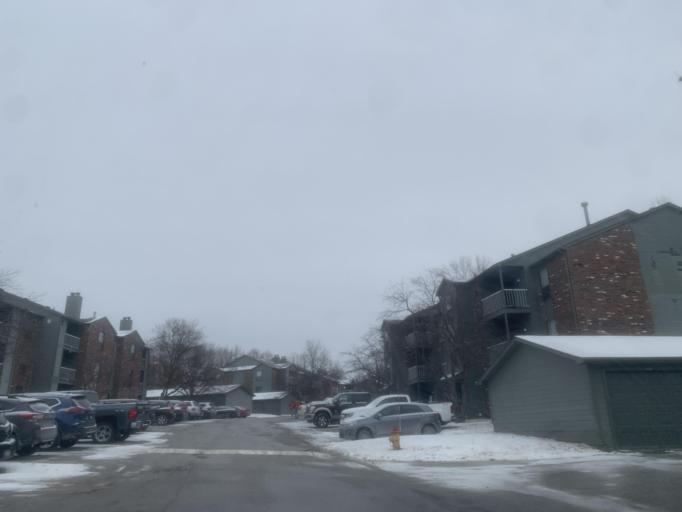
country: US
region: Nebraska
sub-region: Douglas County
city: Ralston
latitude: 41.2722
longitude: -96.0842
